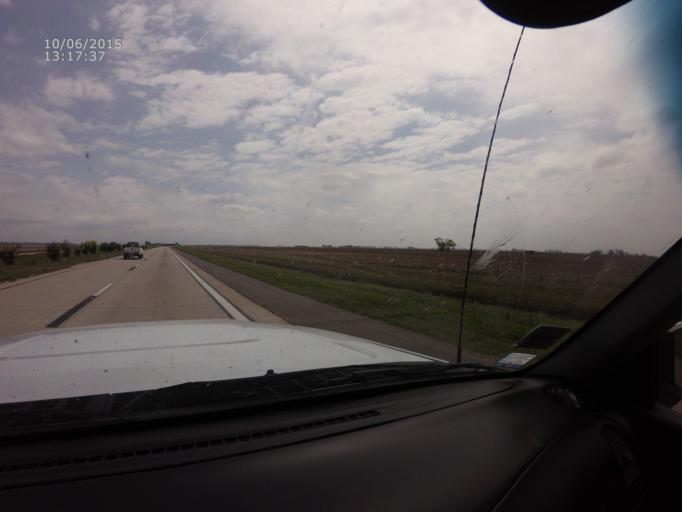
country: AR
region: Cordoba
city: General Roca
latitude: -32.6878
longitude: -61.9963
